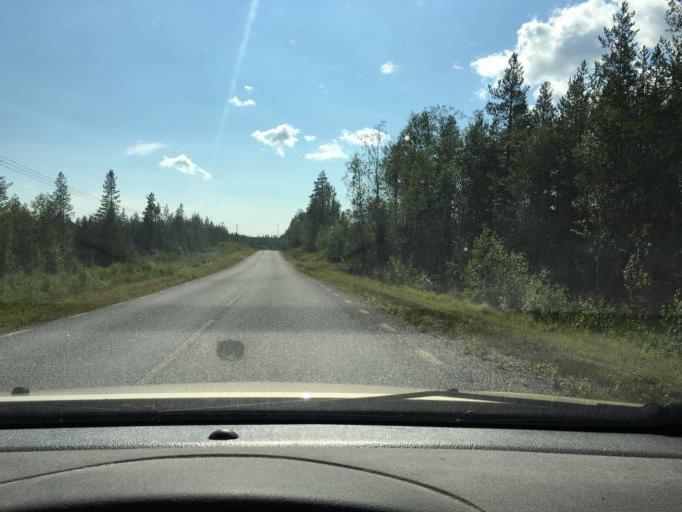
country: SE
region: Norrbotten
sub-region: Kalix Kommun
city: Toere
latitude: 66.0601
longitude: 22.6019
